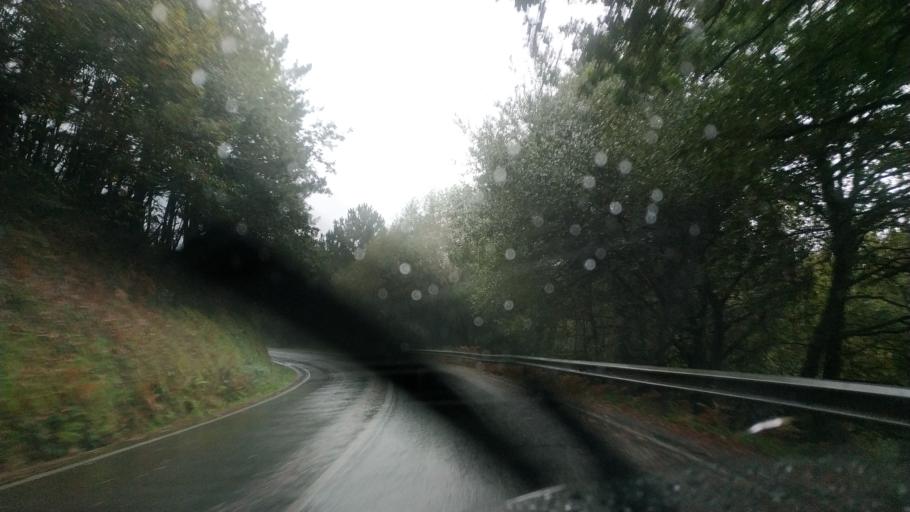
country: ES
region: Galicia
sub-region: Provincia da Coruna
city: Negreira
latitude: 42.9112
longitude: -8.7520
